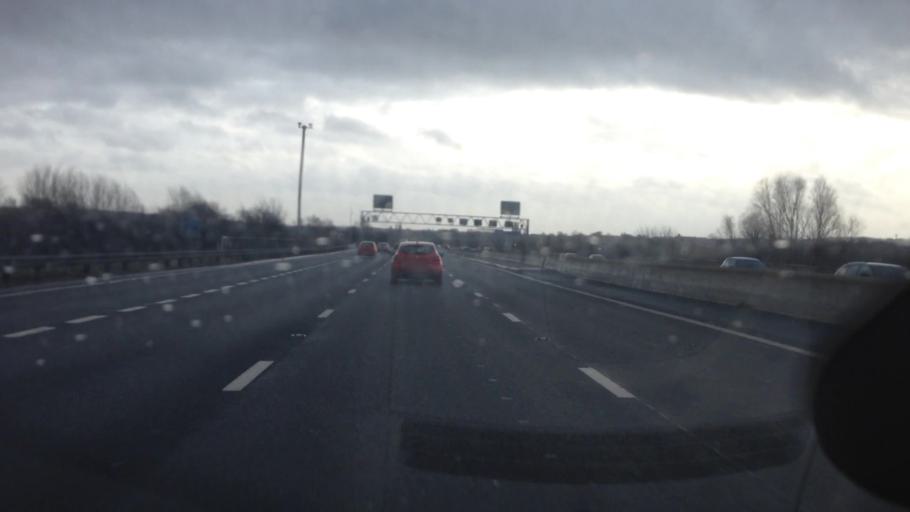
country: GB
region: England
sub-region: City and Borough of Wakefield
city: Crigglestone
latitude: 53.6598
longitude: -1.5321
